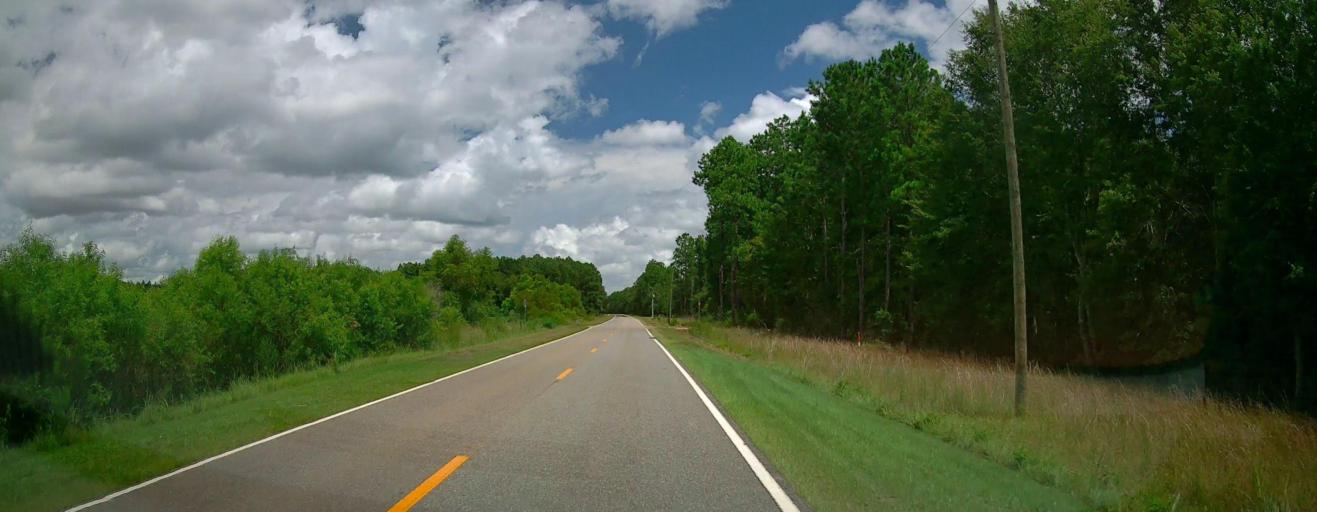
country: US
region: Georgia
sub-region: Irwin County
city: Ocilla
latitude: 31.6455
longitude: -83.3223
